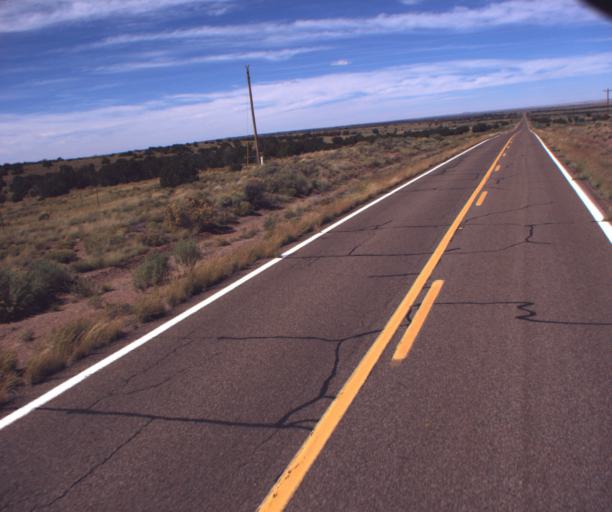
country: US
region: Arizona
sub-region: Apache County
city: Saint Johns
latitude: 34.5590
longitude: -109.6280
